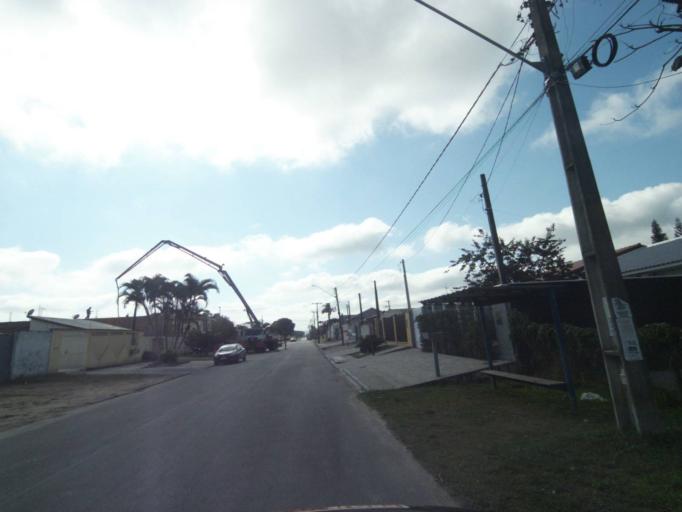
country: BR
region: Parana
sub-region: Paranagua
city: Paranagua
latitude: -25.5483
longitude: -48.5399
